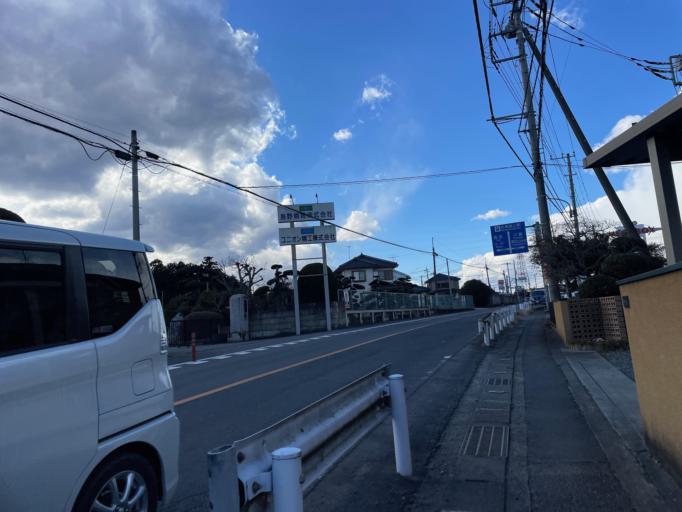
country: JP
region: Saitama
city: Ogawa
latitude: 36.0374
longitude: 139.3370
